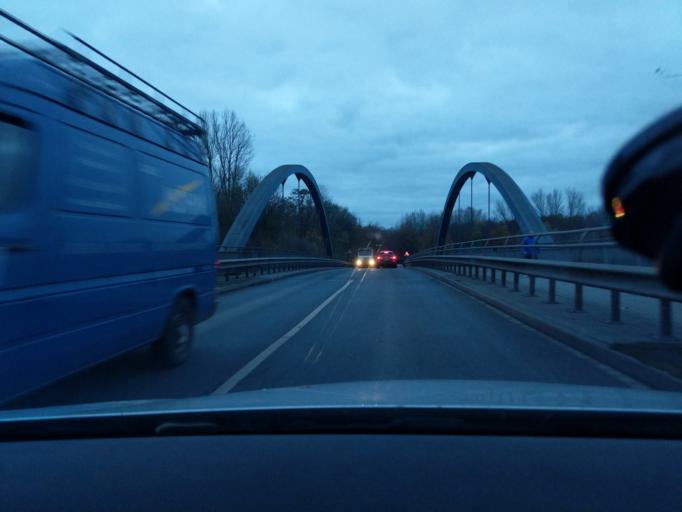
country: DE
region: North Rhine-Westphalia
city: Lunen
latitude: 51.6059
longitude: 7.4793
